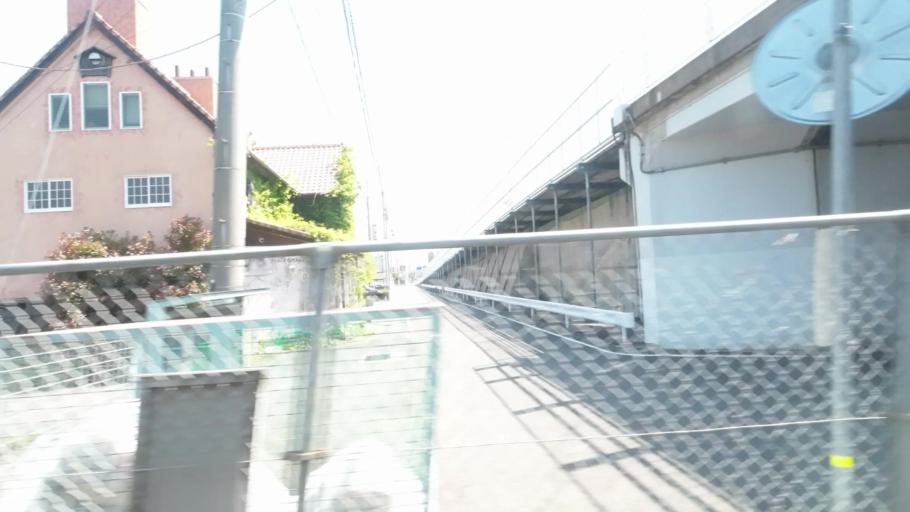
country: JP
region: Ehime
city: Saijo
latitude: 33.9276
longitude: 133.0874
